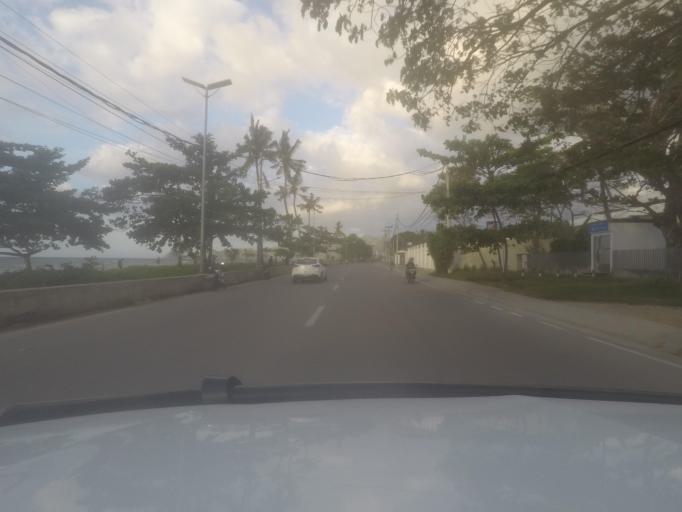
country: TL
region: Dili
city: Dili
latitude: -8.5482
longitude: 125.5623
